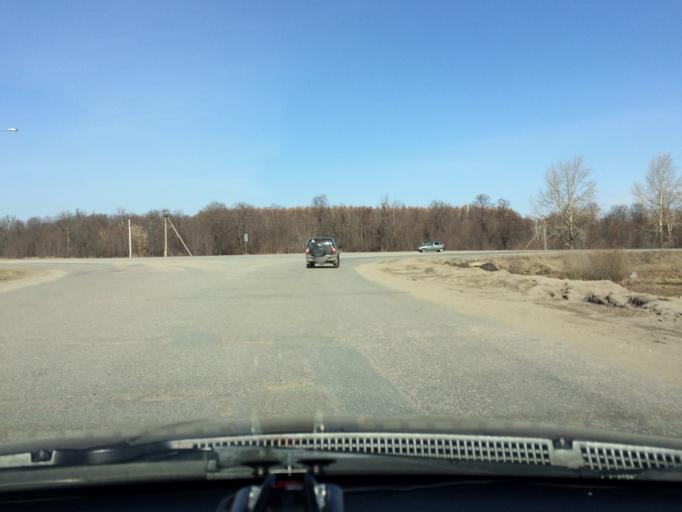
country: RU
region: Mariy-El
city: Yoshkar-Ola
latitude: 56.6455
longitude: 47.9378
